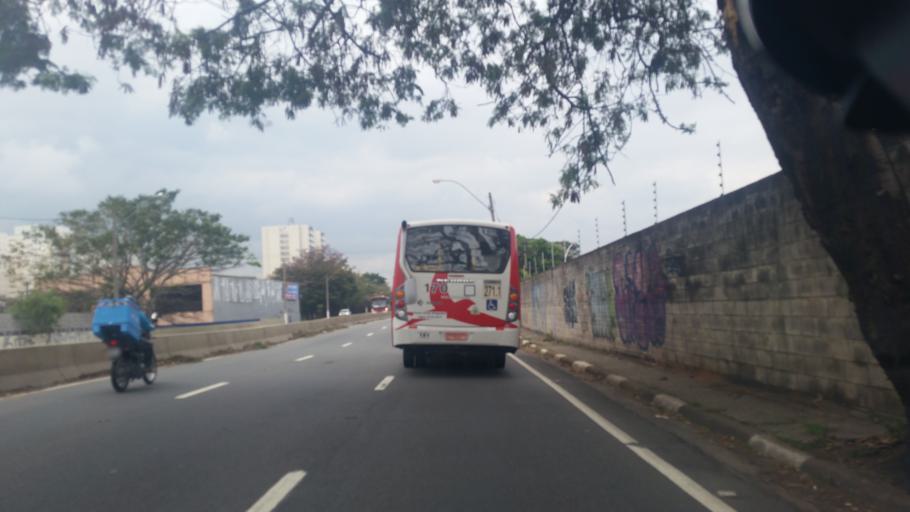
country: BR
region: Sao Paulo
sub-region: Campinas
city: Campinas
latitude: -22.9026
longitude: -47.0794
